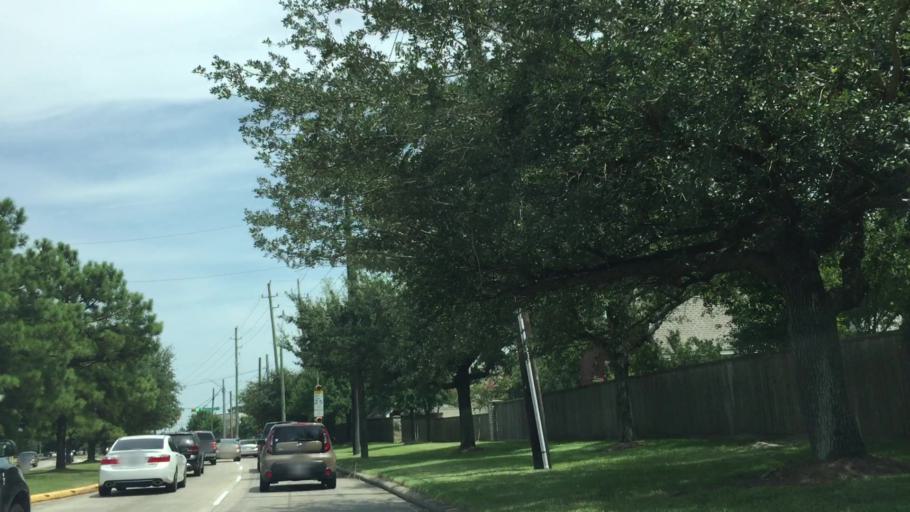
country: US
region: Texas
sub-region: Harris County
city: Jersey Village
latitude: 29.9042
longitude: -95.5589
